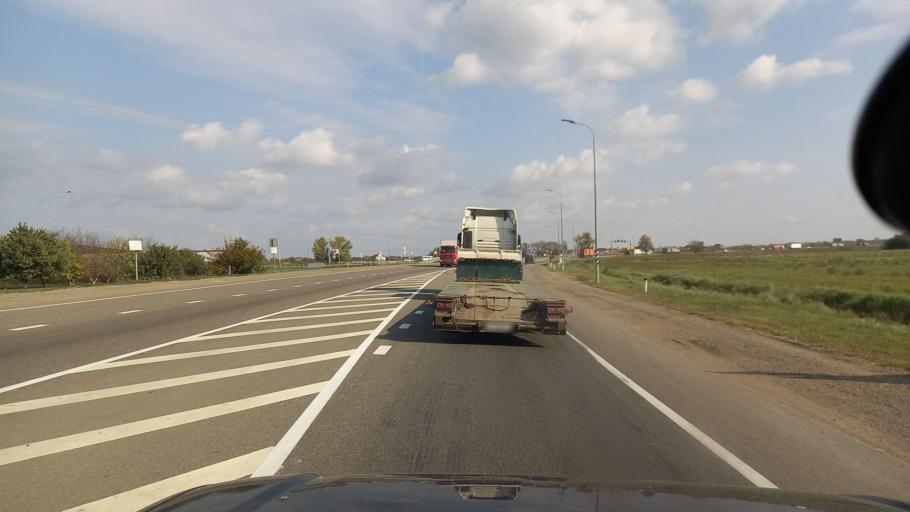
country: RU
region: Krasnodarskiy
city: Abinsk
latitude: 44.8572
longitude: 38.1891
